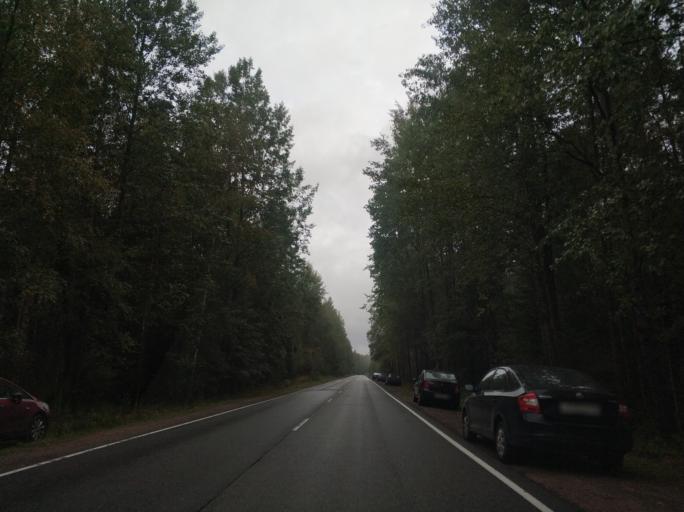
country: RU
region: Leningrad
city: Borisova Griva
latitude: 60.1563
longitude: 30.9293
